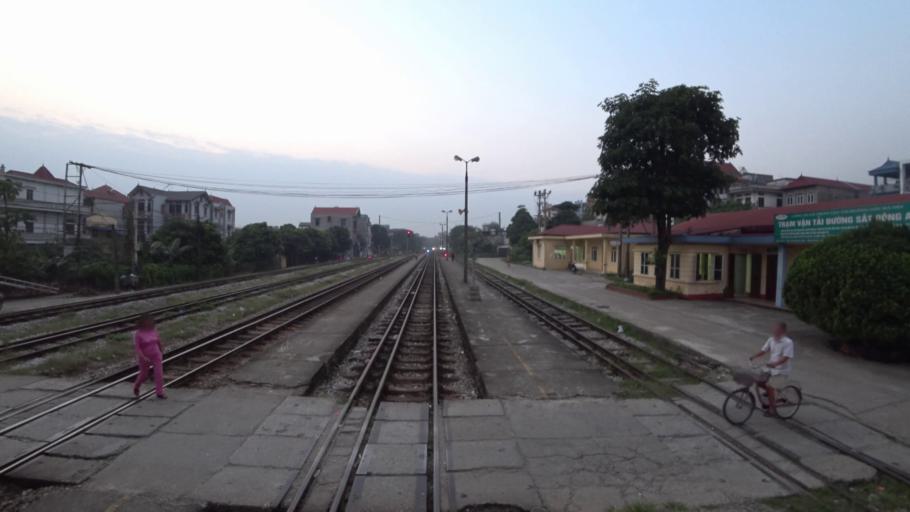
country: VN
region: Ha Noi
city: Soc Son
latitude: 21.2260
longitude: 105.8610
